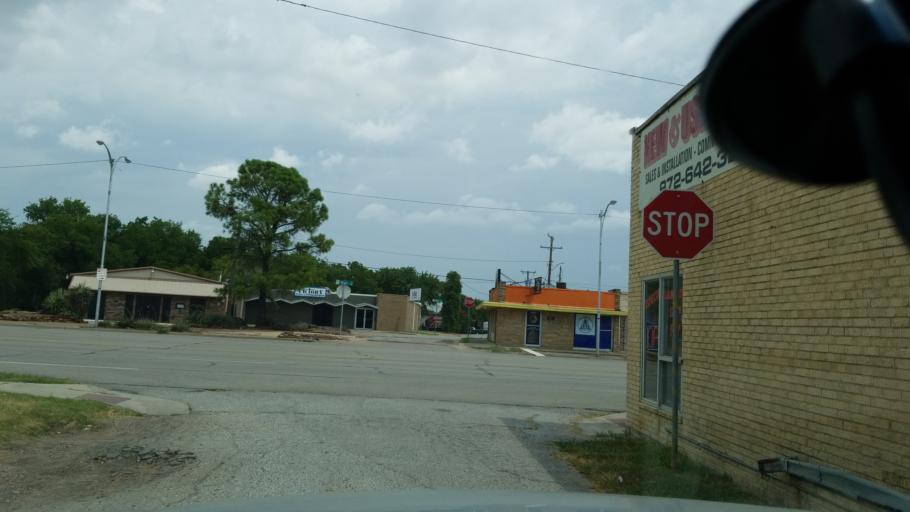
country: US
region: Texas
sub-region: Dallas County
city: Grand Prairie
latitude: 32.7456
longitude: -96.9968
